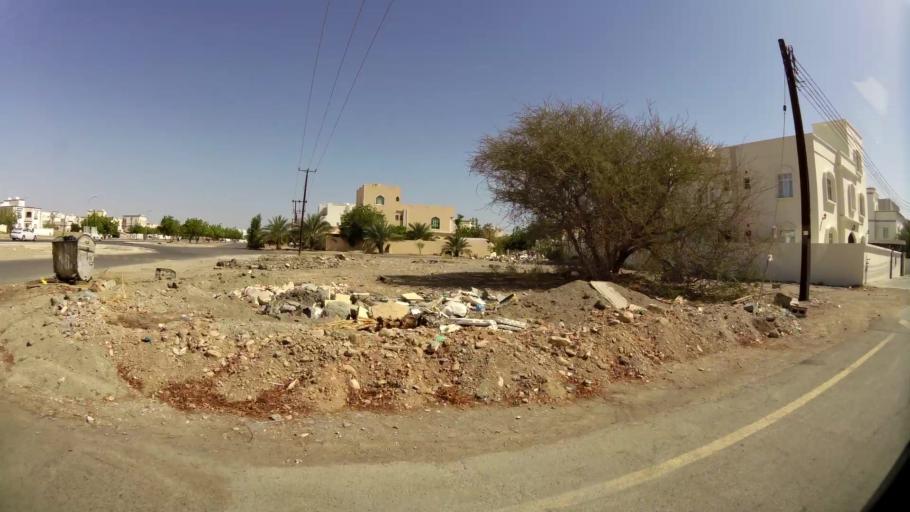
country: OM
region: Muhafazat Masqat
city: As Sib al Jadidah
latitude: 23.6043
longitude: 58.2378
